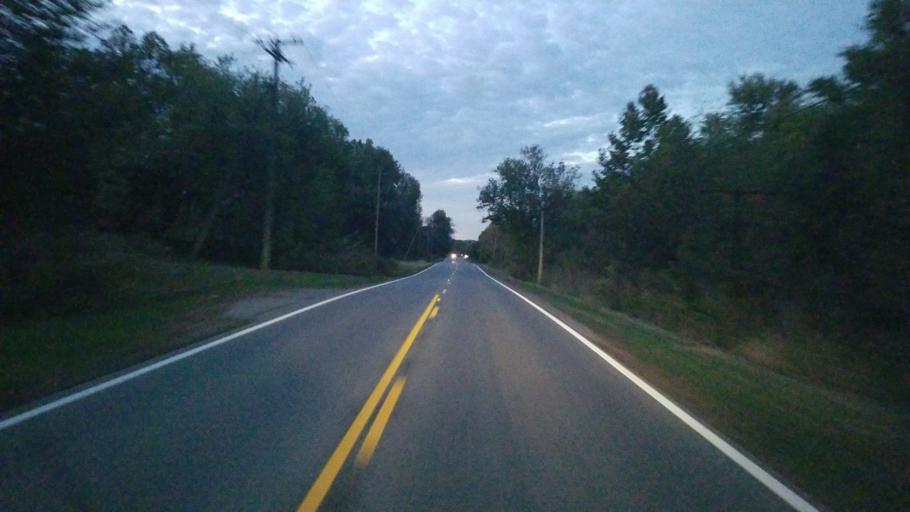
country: US
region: Ohio
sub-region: Scioto County
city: Rosemount
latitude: 38.8124
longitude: -83.0093
